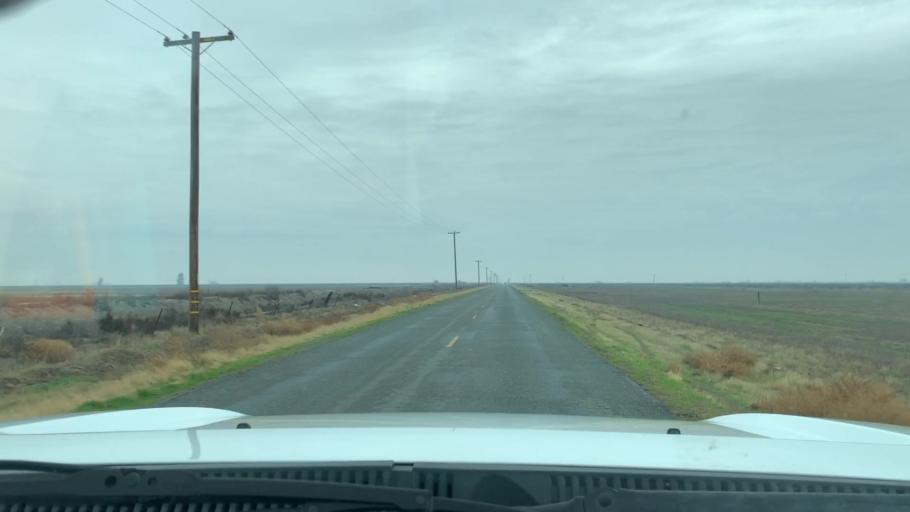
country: US
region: California
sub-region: Tulare County
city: Alpaugh
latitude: 35.7609
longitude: -119.4875
